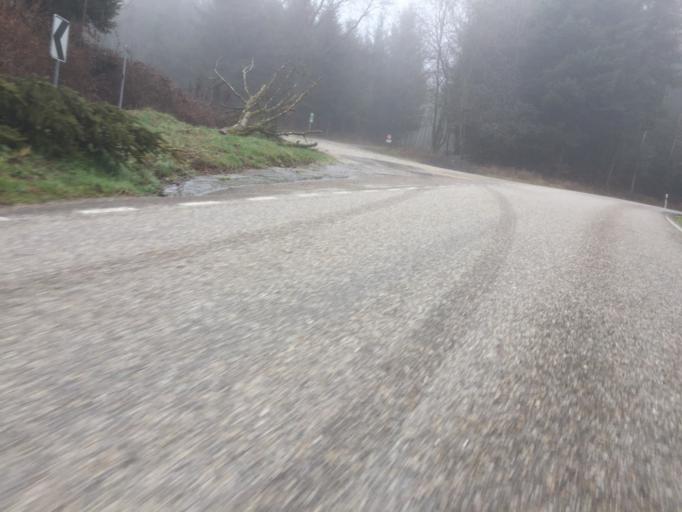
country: CH
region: Bern
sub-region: Seeland District
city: Grossaffoltern
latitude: 47.0930
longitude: 7.3704
